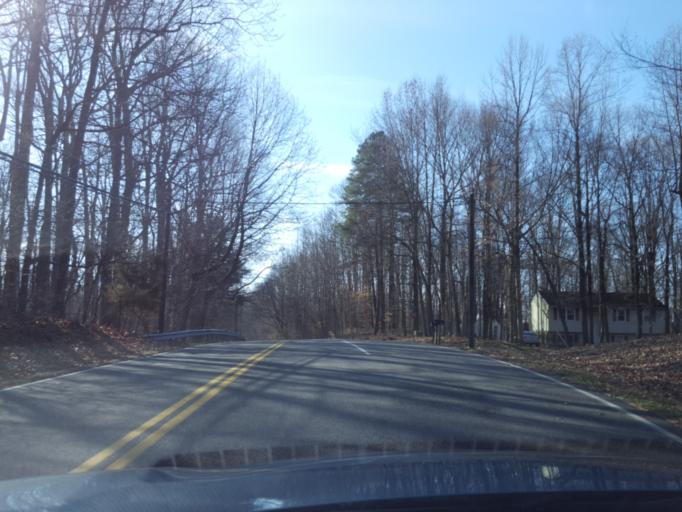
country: US
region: Maryland
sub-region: Calvert County
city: Chesapeake Beach
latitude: 38.6193
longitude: -76.5301
